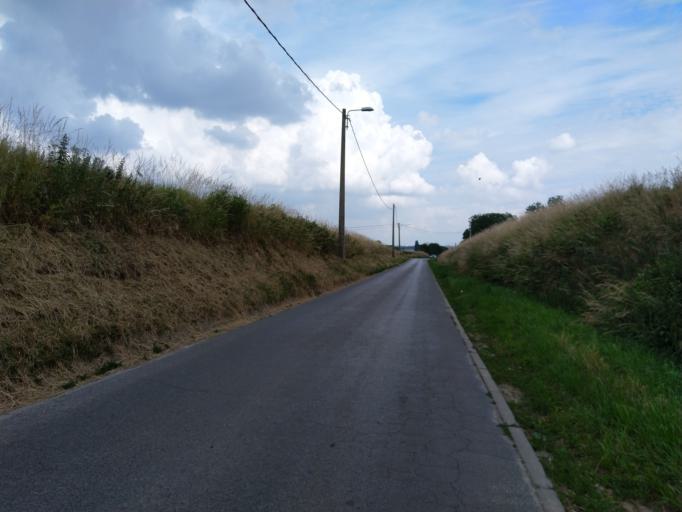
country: FR
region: Nord-Pas-de-Calais
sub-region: Departement du Nord
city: Boussois
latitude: 50.3703
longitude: 4.0274
